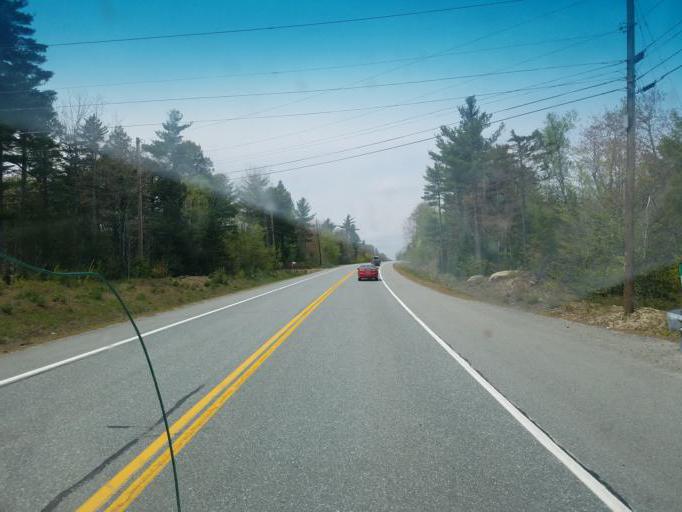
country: US
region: Maine
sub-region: Hancock County
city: Ellsworth
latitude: 44.5842
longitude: -68.4912
